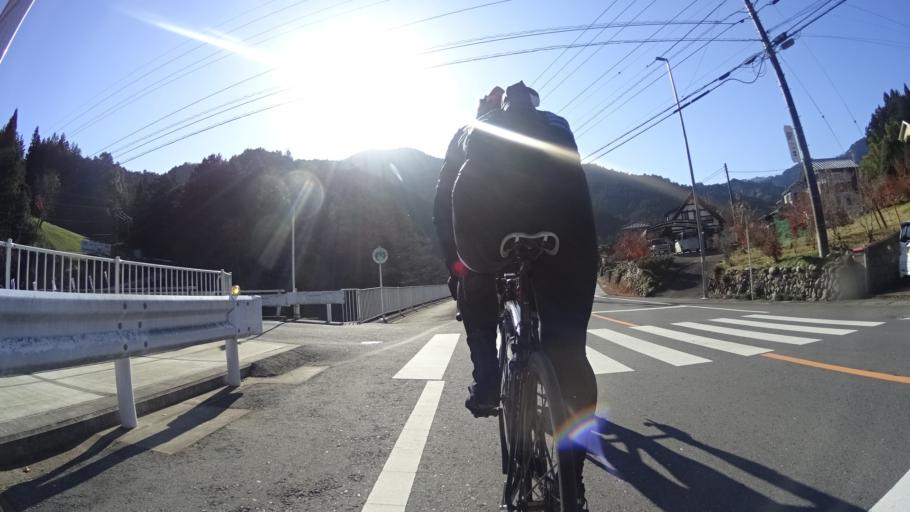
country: JP
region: Tokyo
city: Ome
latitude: 35.8539
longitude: 139.2040
